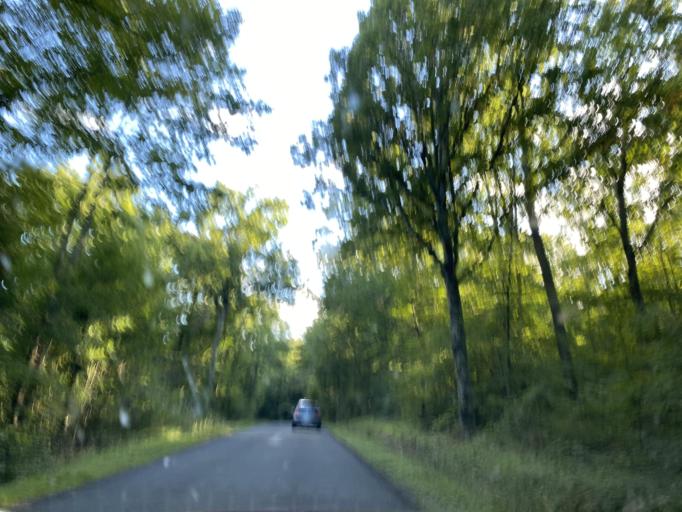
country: FR
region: Auvergne
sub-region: Departement du Puy-de-Dome
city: Saint-Sylvestre-Pragoulin
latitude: 46.0132
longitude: 3.3952
